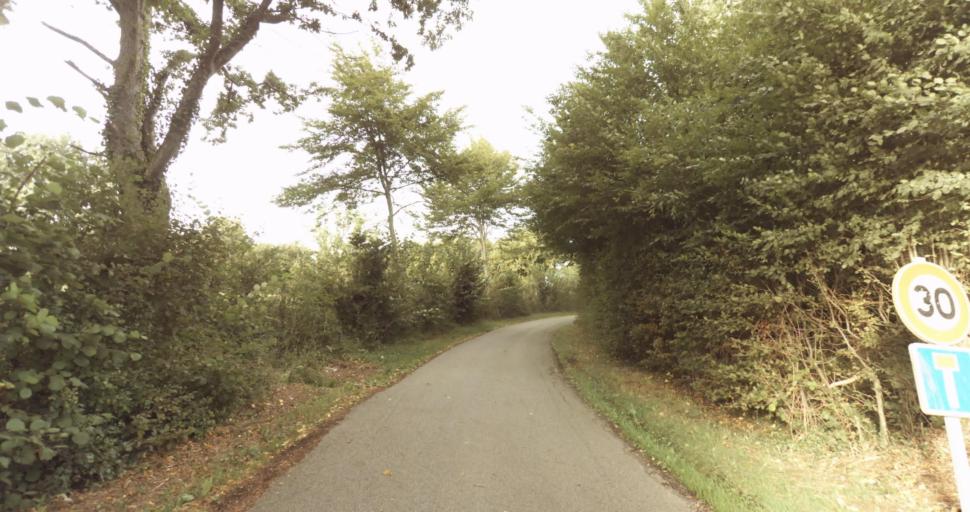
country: FR
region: Lower Normandy
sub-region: Departement de l'Orne
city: Sainte-Gauburge-Sainte-Colombe
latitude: 48.7216
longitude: 0.4248
